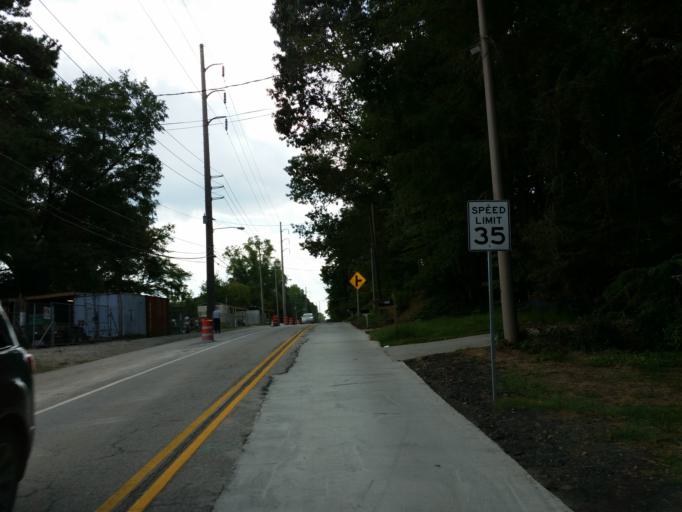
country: US
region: Georgia
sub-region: Fulton County
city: Atlanta
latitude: 33.8164
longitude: -84.4078
